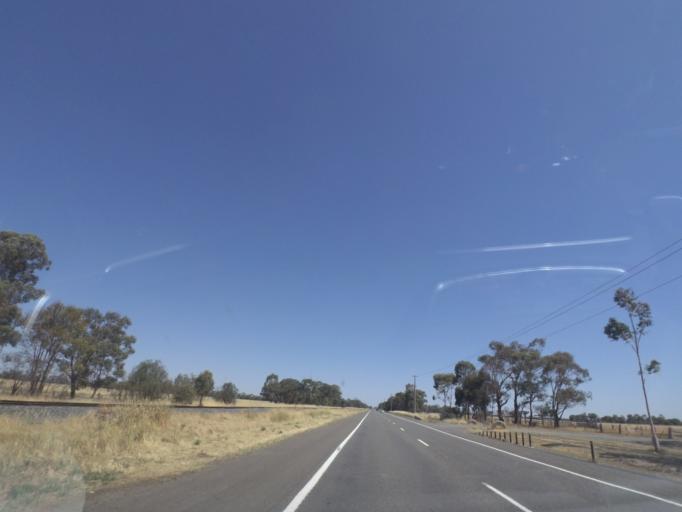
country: AU
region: Victoria
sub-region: Greater Shepparton
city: Shepparton
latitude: -36.2447
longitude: 145.4319
